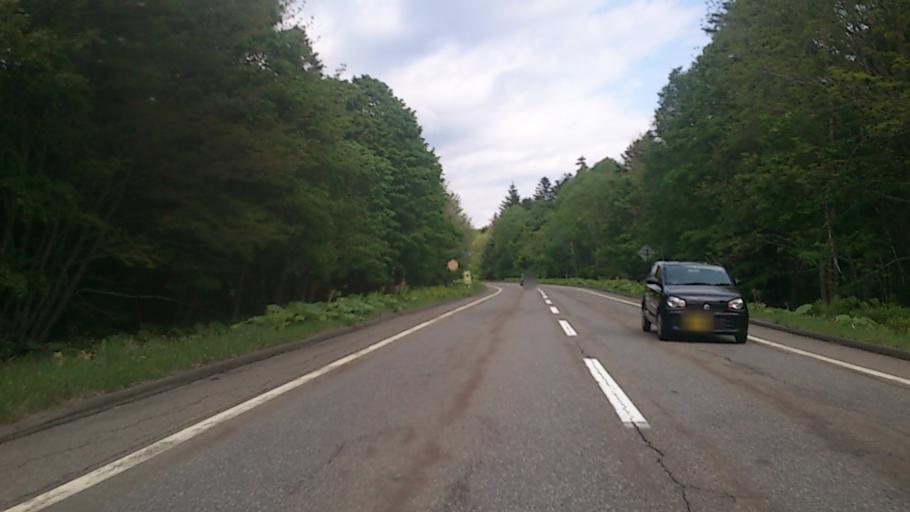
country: JP
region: Hokkaido
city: Kitami
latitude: 43.4076
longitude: 143.9508
